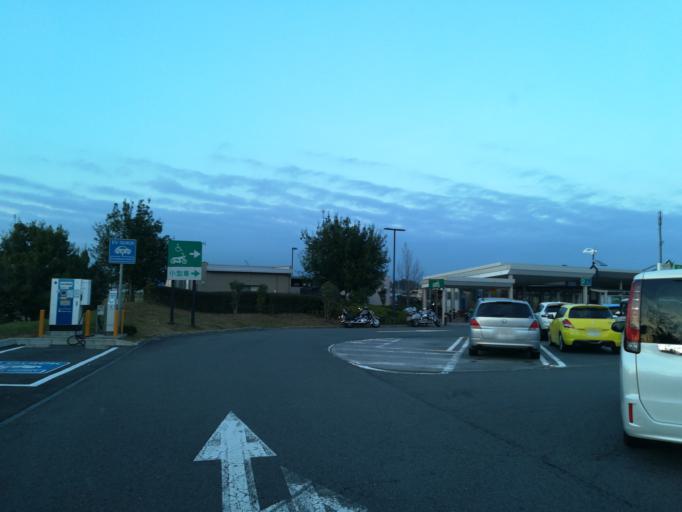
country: JP
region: Gunma
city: Isesaki
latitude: 36.3541
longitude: 139.1885
